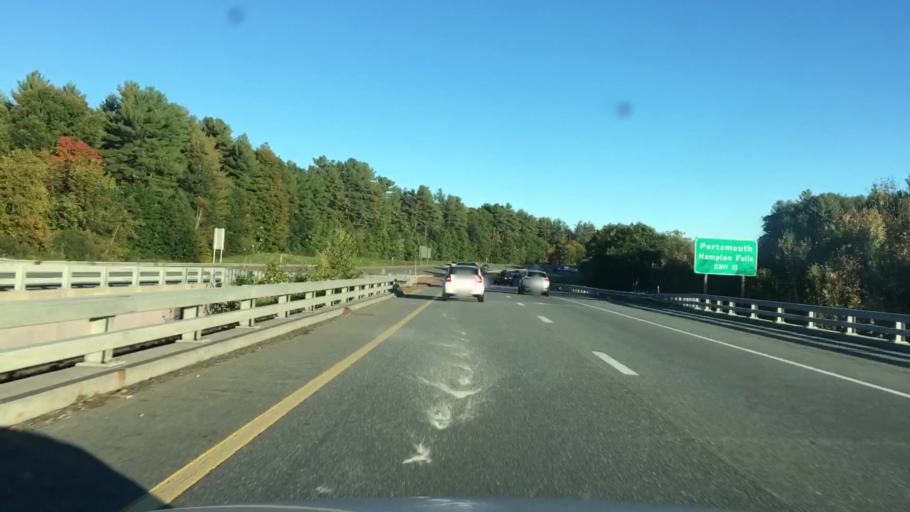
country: US
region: New Hampshire
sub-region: Rockingham County
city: Exeter
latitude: 42.9996
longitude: -70.9377
